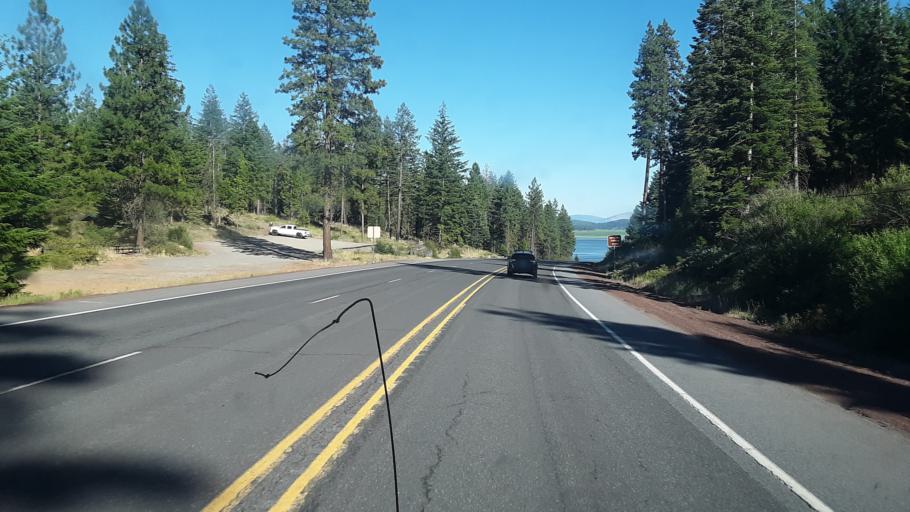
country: US
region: Oregon
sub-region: Klamath County
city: Klamath Falls
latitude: 42.3262
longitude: -121.9510
